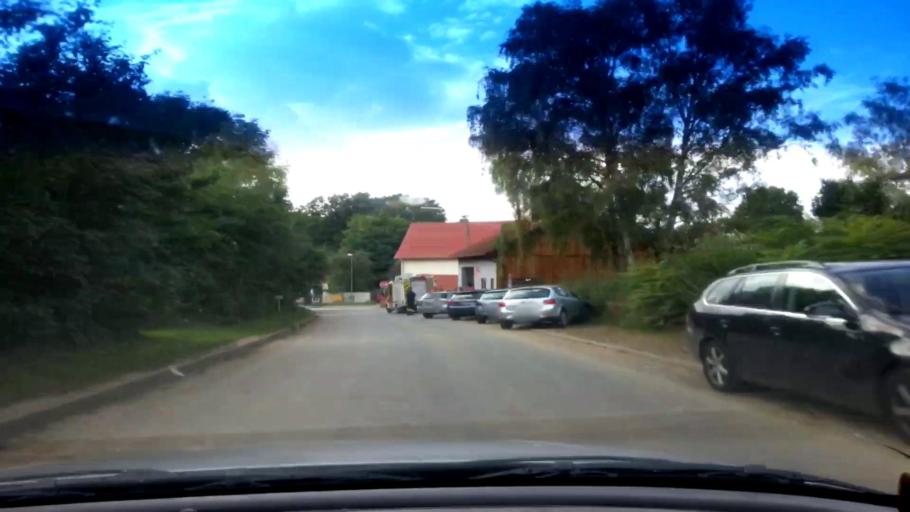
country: DE
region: Bavaria
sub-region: Upper Franconia
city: Schesslitz
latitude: 49.9599
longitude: 11.0035
